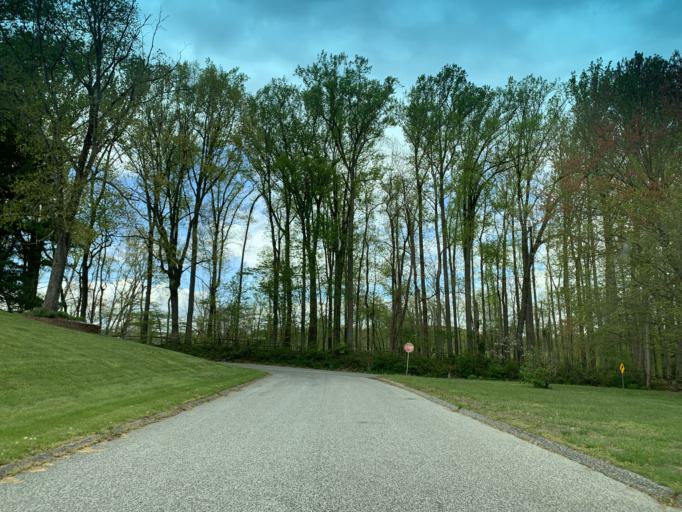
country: US
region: Maryland
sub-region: Harford County
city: Bel Air
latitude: 39.5010
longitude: -76.3611
